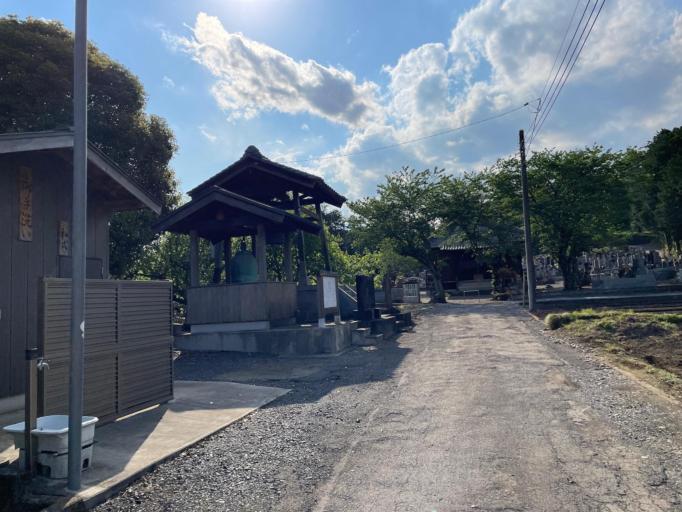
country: JP
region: Tochigi
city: Tochigi
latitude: 36.4150
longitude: 139.7122
